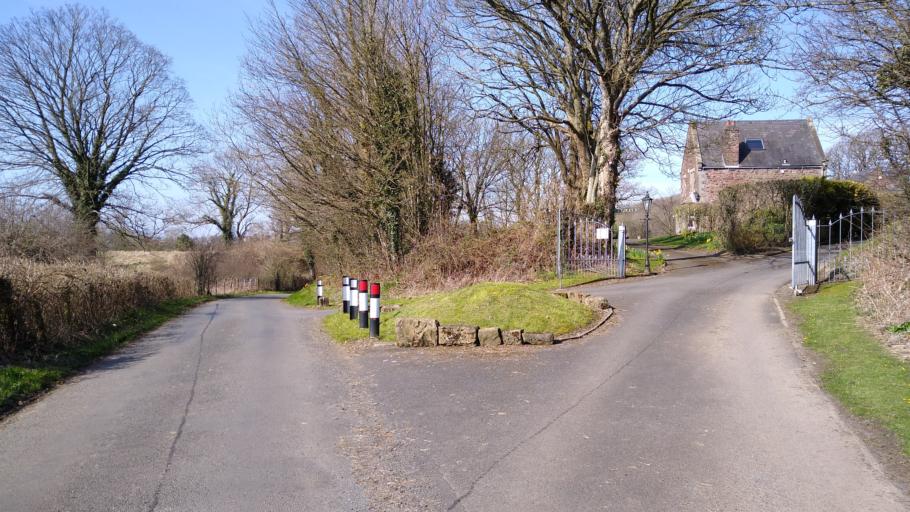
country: GB
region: England
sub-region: Cumbria
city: Cockermouth
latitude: 54.6703
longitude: -3.4104
